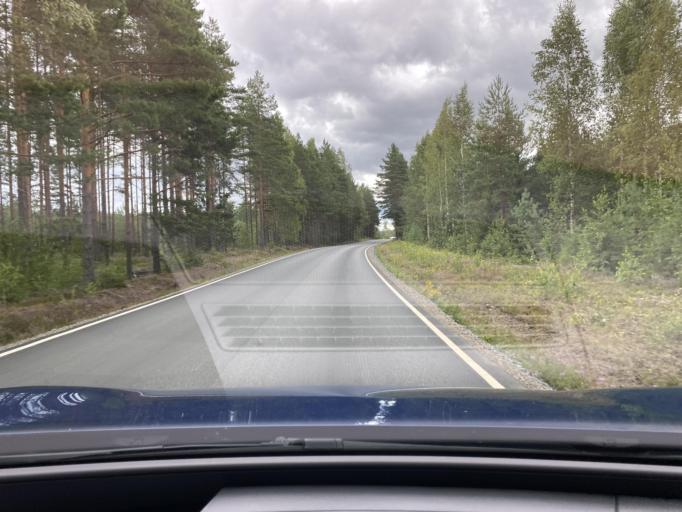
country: FI
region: Pirkanmaa
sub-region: Lounais-Pirkanmaa
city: Vammala
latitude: 61.2847
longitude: 23.0296
